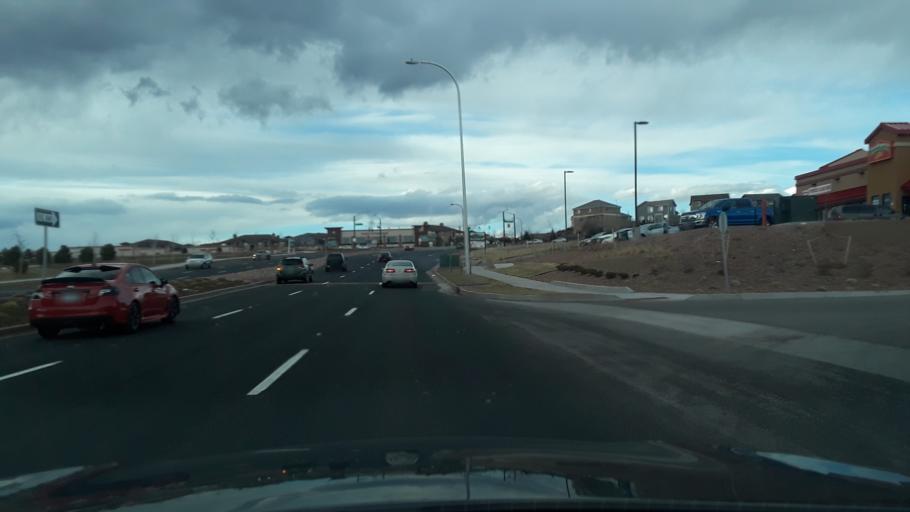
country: US
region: Colorado
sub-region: El Paso County
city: Gleneagle
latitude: 38.9997
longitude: -104.7978
